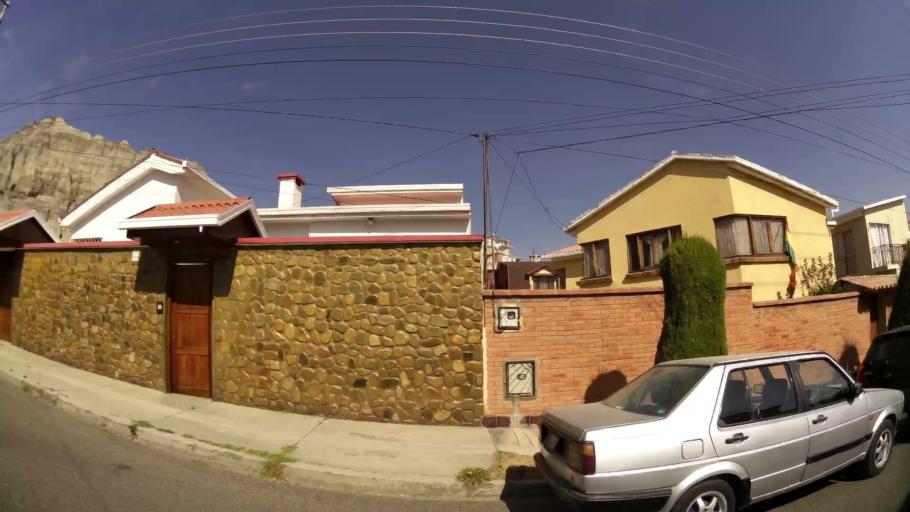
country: BO
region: La Paz
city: La Paz
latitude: -16.5322
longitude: -68.0711
